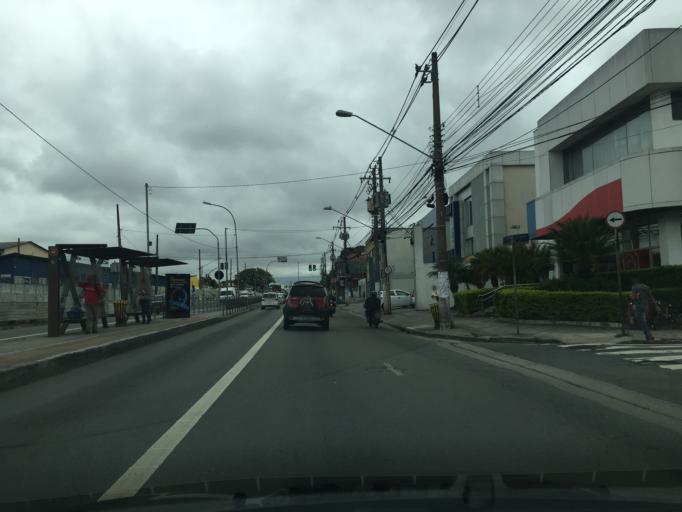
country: BR
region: Sao Paulo
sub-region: Taboao Da Serra
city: Taboao da Serra
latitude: -23.5908
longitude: -46.7306
